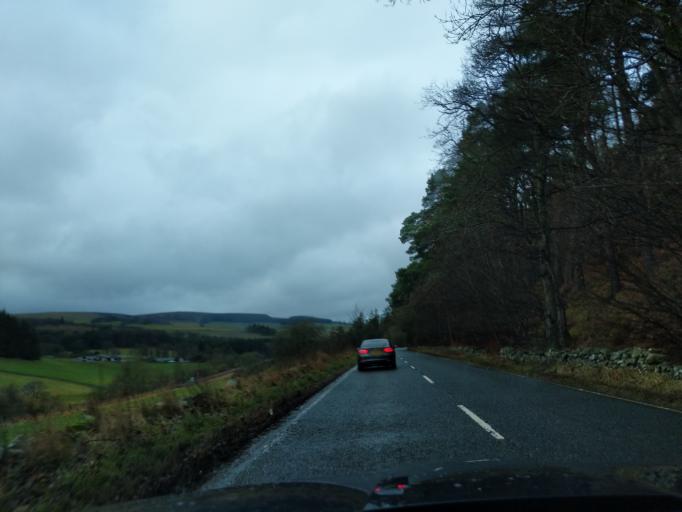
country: GB
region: Scotland
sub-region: The Scottish Borders
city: Galashiels
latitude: 55.6469
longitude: -2.8572
